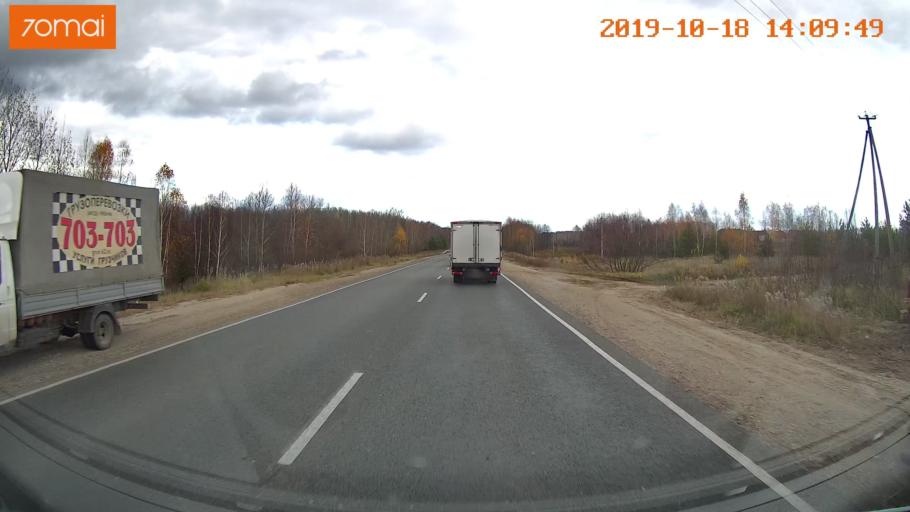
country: RU
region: Rjazan
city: Spas-Klepiki
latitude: 55.1439
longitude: 40.1933
